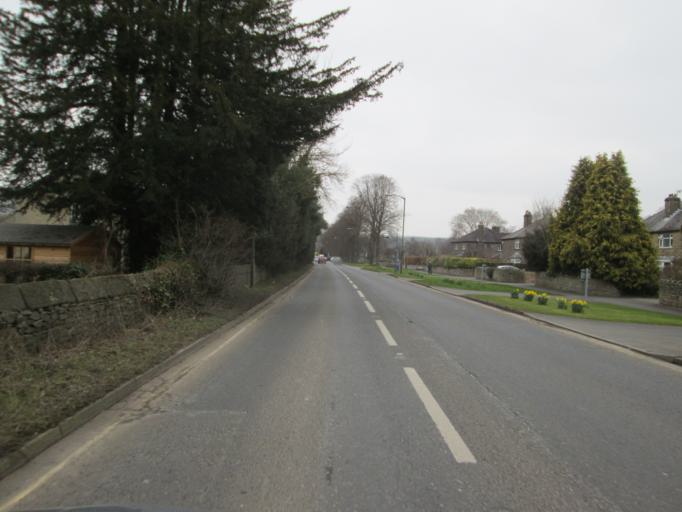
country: GB
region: England
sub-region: Derbyshire
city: Bakewell
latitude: 53.2078
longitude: -1.6696
